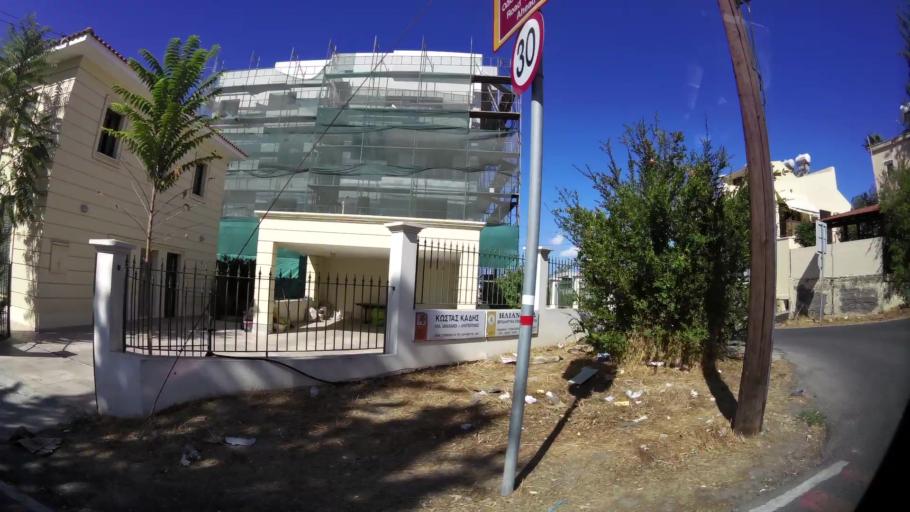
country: CY
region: Lefkosia
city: Nicosia
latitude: 35.1407
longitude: 33.3481
